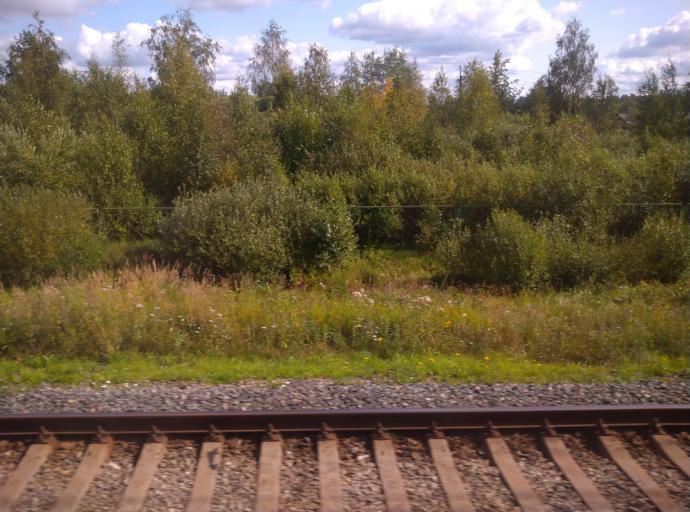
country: RU
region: Leningrad
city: Ul'yanovka
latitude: 59.6292
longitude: 30.7656
